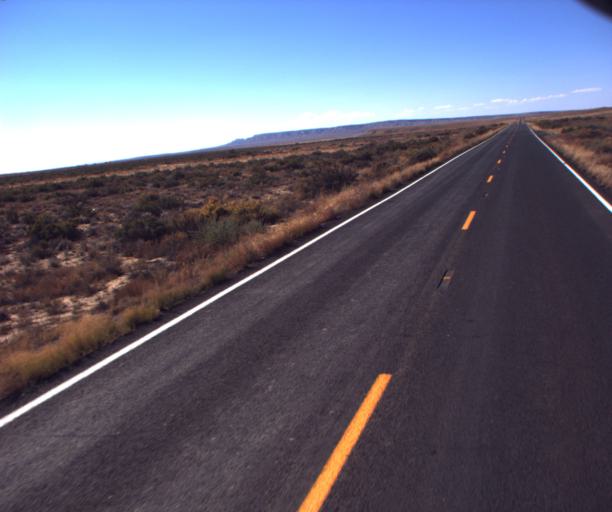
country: US
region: Arizona
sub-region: Navajo County
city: First Mesa
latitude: 35.9811
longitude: -110.7287
